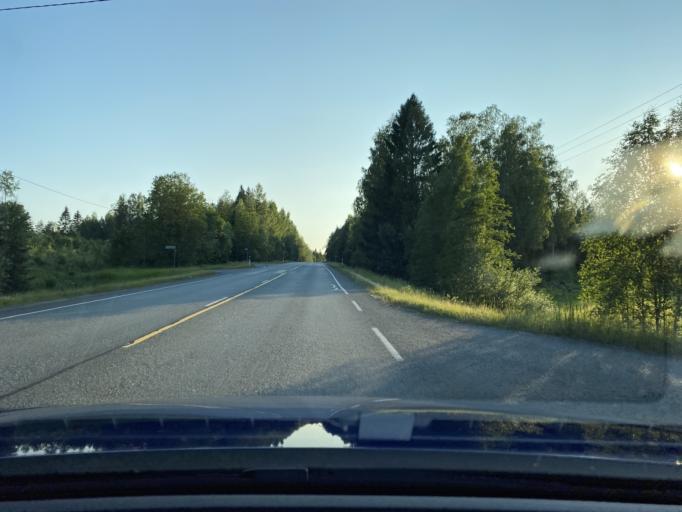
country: FI
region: Haeme
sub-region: Forssa
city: Tammela
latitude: 60.8269
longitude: 23.9189
